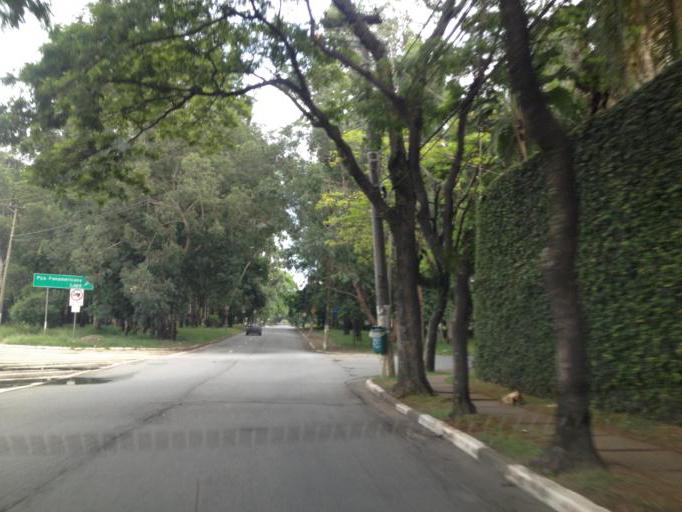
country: BR
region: Sao Paulo
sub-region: Sao Paulo
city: Sao Paulo
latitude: -23.5608
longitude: -46.7056
